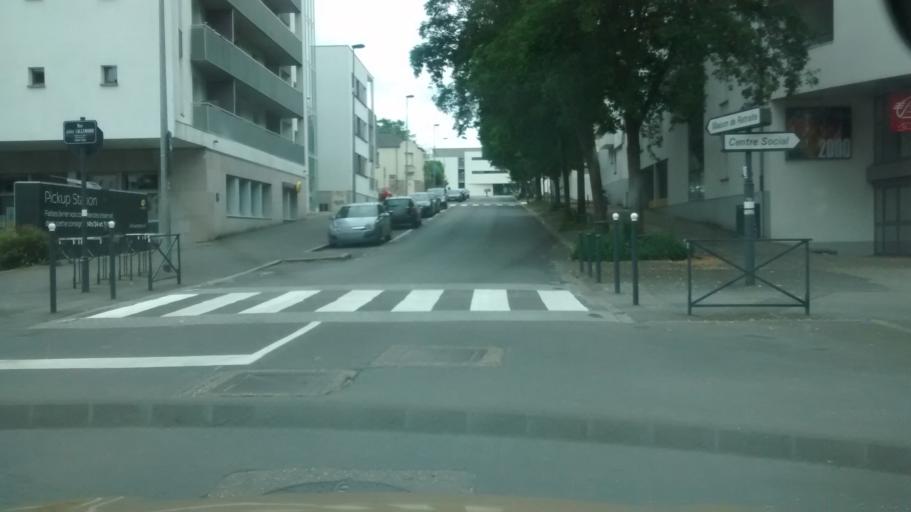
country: FR
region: Brittany
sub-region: Departement d'Ille-et-Vilaine
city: Rennes
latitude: 48.1005
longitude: -1.7069
